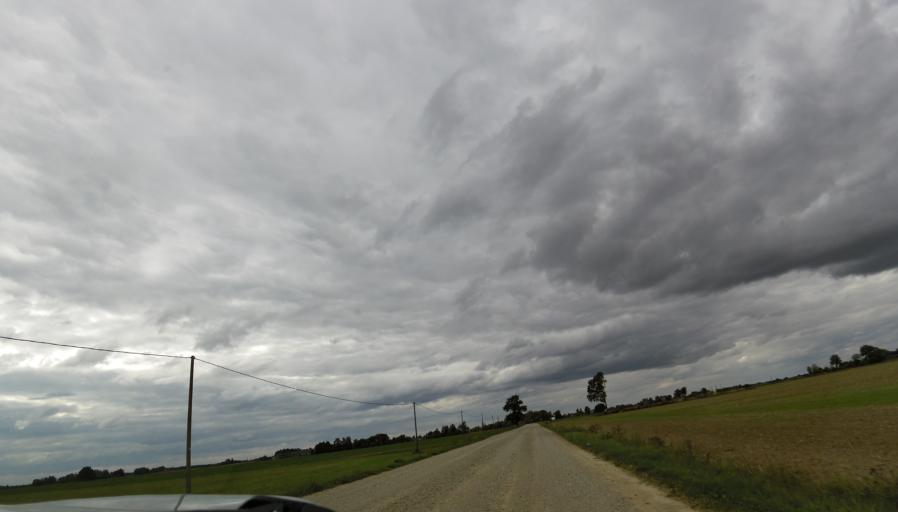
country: LT
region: Panevezys
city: Pasvalys
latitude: 56.0602
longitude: 24.2305
